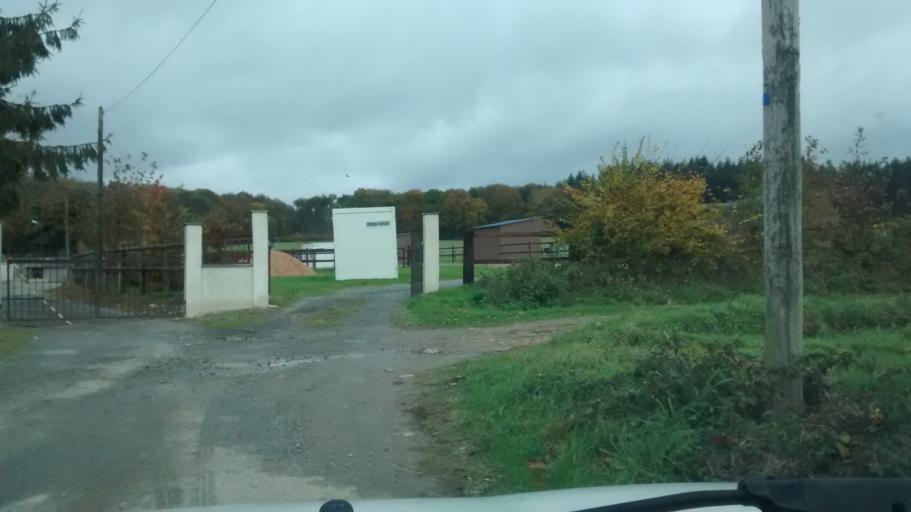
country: FR
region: Brittany
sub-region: Departement d'Ille-et-Vilaine
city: Servon-sur-Vilaine
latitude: 48.1354
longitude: -1.4424
